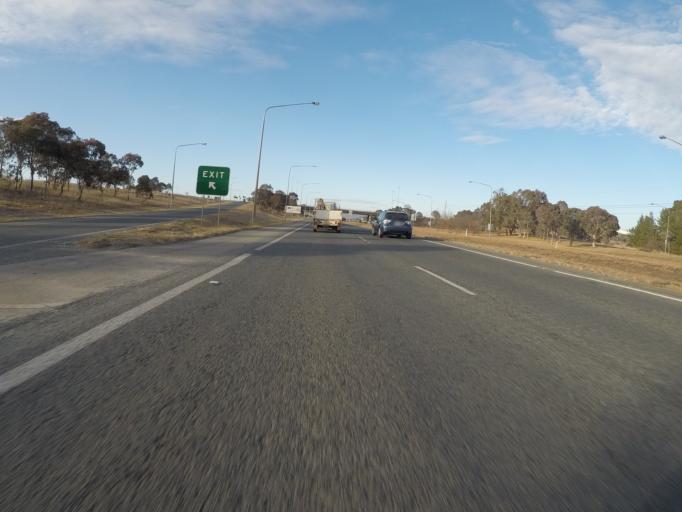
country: AU
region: Australian Capital Territory
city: Forrest
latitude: -35.3381
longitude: 149.1627
